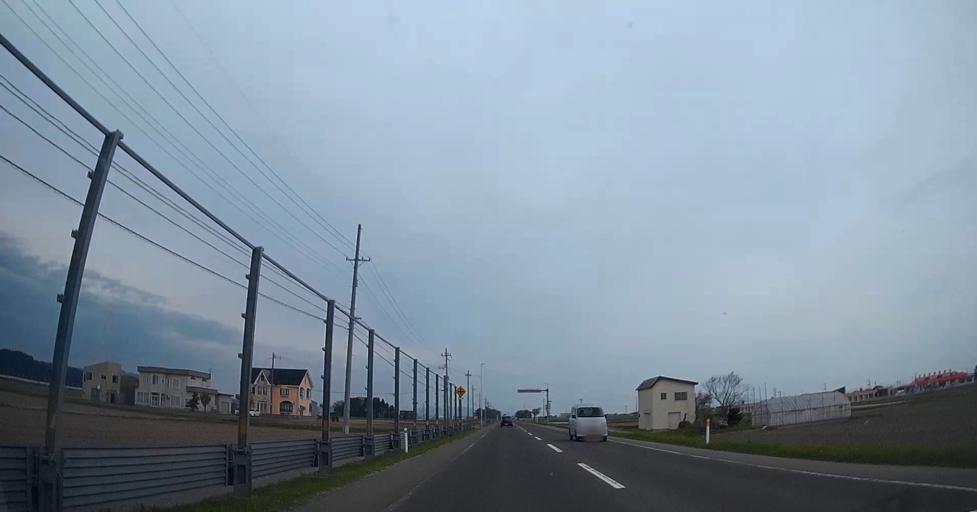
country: JP
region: Aomori
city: Aomori Shi
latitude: 40.8870
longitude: 140.6698
